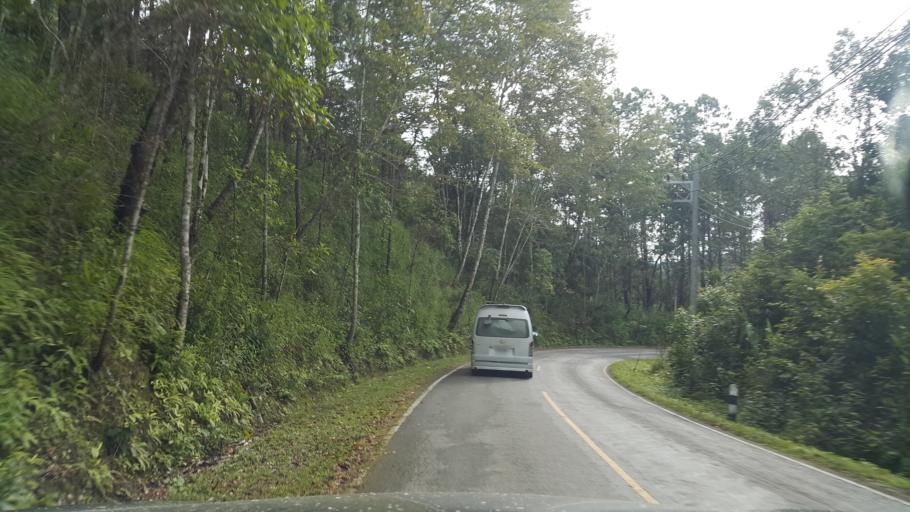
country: TH
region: Chiang Mai
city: Chaem Luang
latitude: 18.9327
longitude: 98.4781
